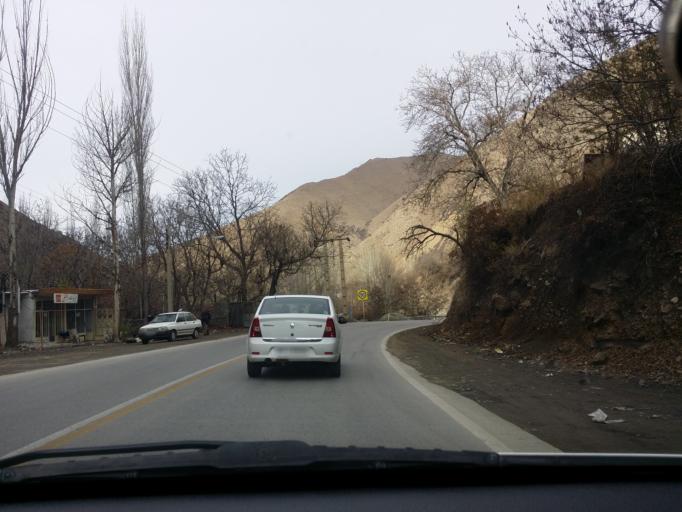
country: IR
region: Tehran
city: Tajrish
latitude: 36.0228
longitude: 51.2604
